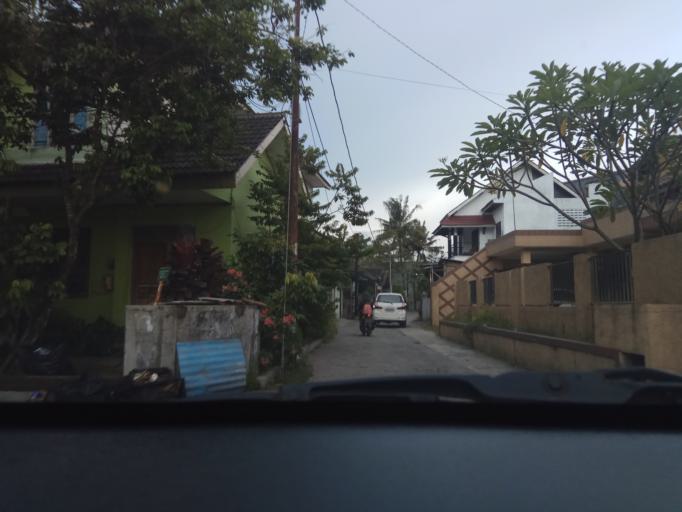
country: ID
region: Daerah Istimewa Yogyakarta
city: Depok
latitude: -7.7609
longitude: 110.4018
